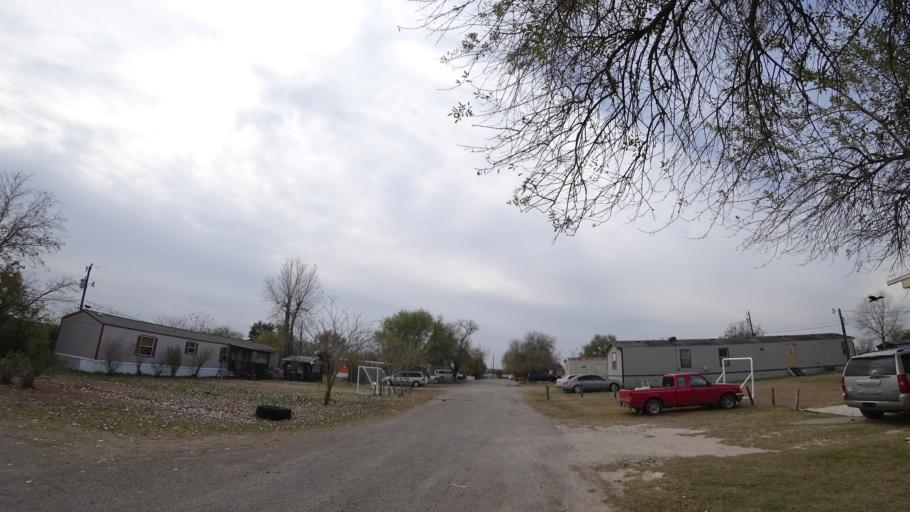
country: US
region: Texas
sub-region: Travis County
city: Garfield
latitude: 30.1485
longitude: -97.6664
